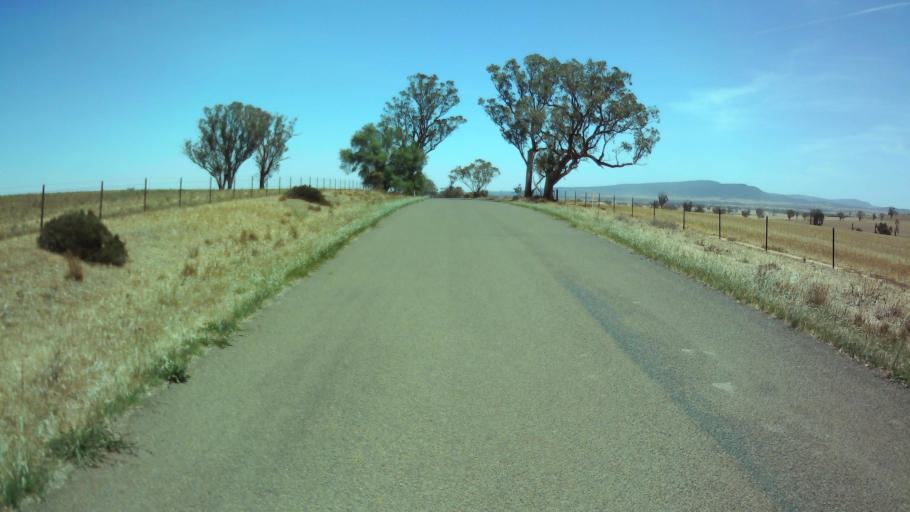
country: AU
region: New South Wales
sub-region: Weddin
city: Grenfell
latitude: -34.0542
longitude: 148.2266
